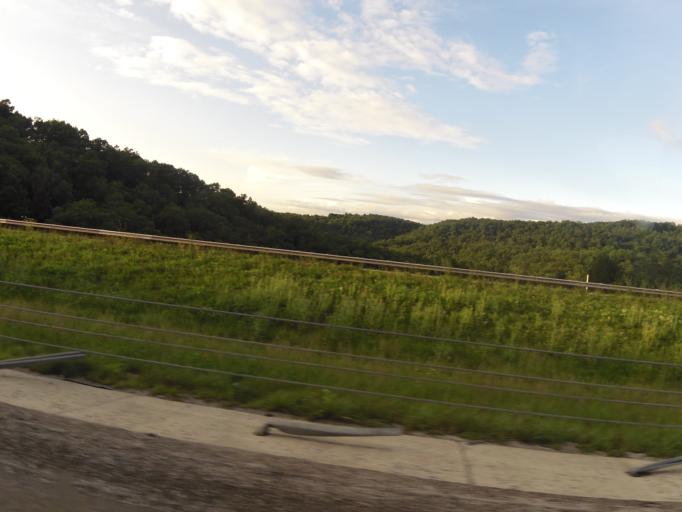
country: US
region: Kentucky
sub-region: Laurel County
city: London
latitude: 37.2148
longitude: -84.1991
